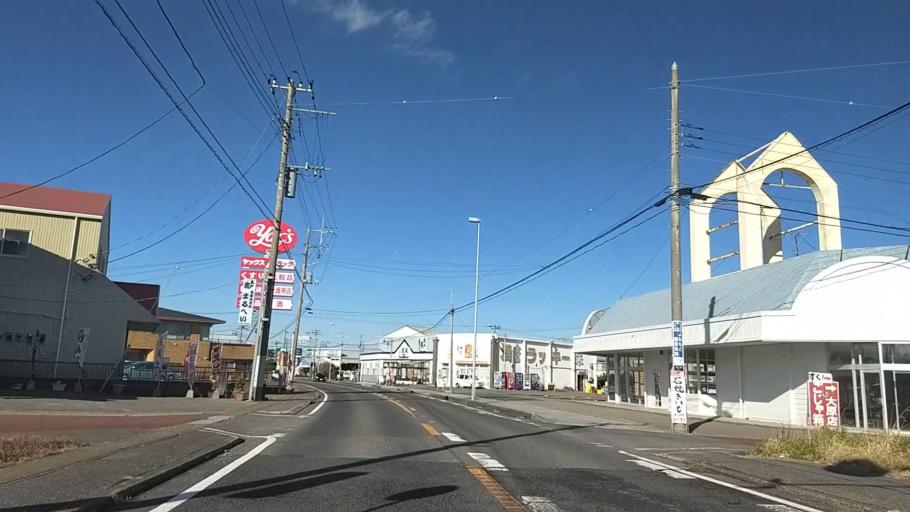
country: JP
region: Chiba
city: Ohara
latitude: 35.2517
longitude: 140.3962
